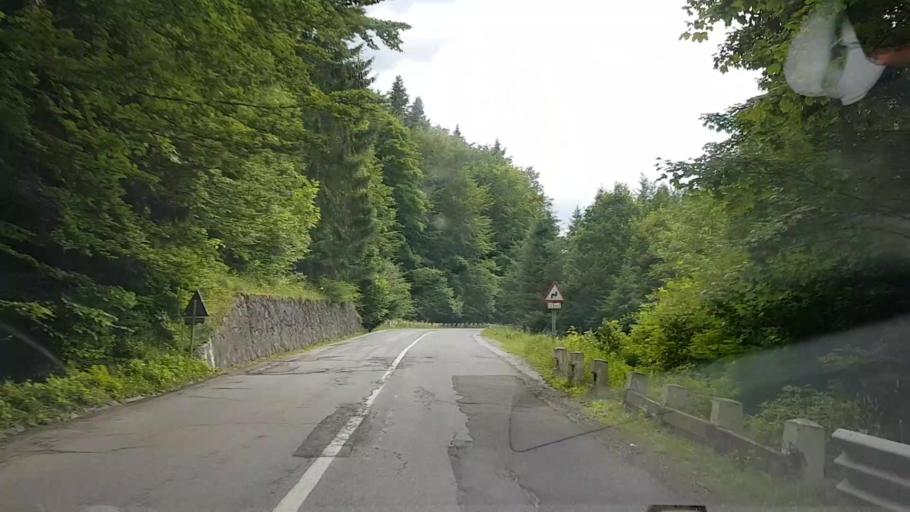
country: RO
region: Neamt
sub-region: Comuna Pangarati
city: Pangarati
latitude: 46.9862
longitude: 26.1171
